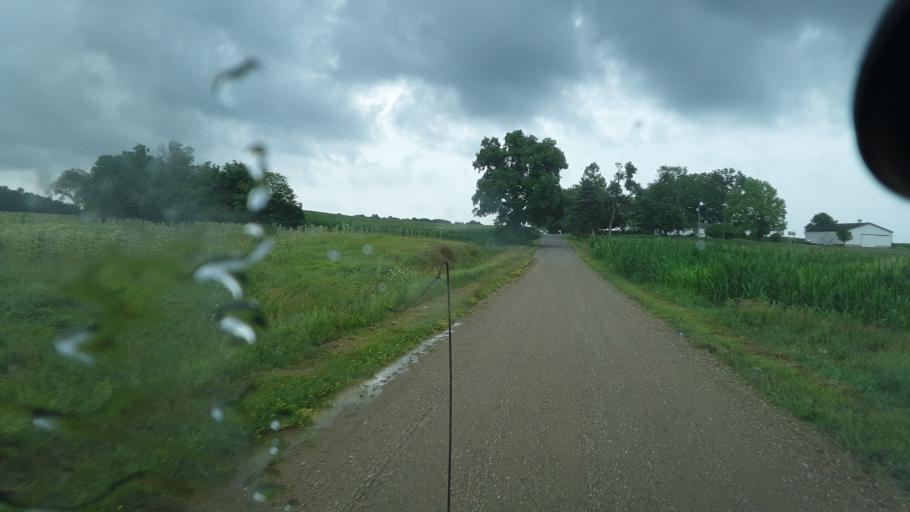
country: US
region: Indiana
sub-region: Steuben County
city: Hamilton
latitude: 41.5377
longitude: -84.8319
